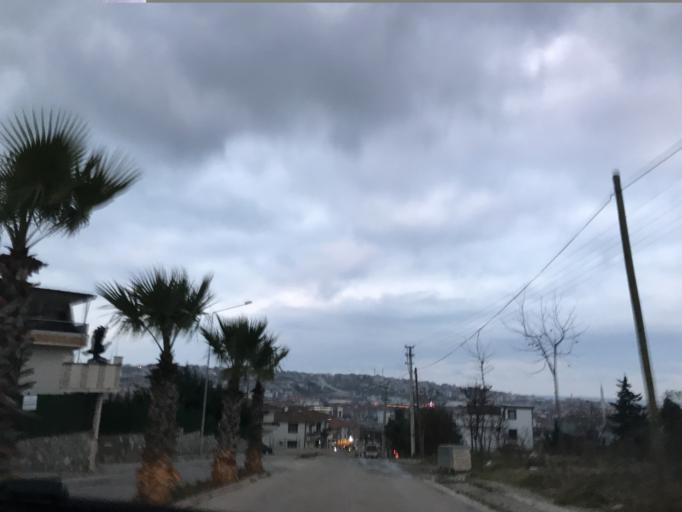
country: TR
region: Yalova
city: Yalova
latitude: 40.6362
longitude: 29.2635
